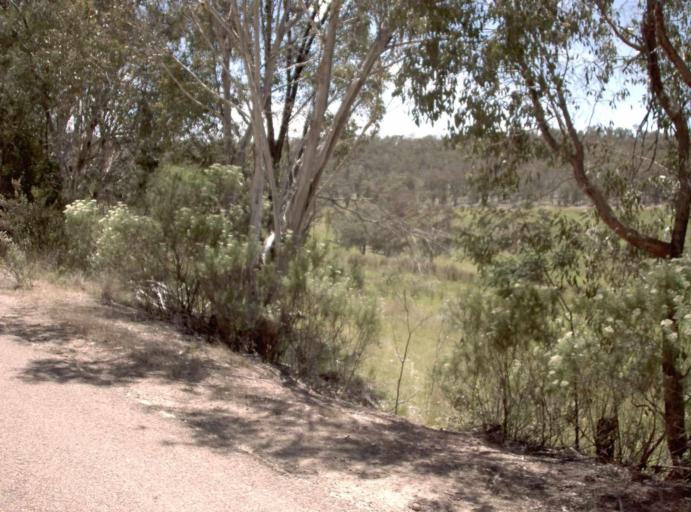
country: AU
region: New South Wales
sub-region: Snowy River
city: Jindabyne
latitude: -37.0467
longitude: 148.2766
